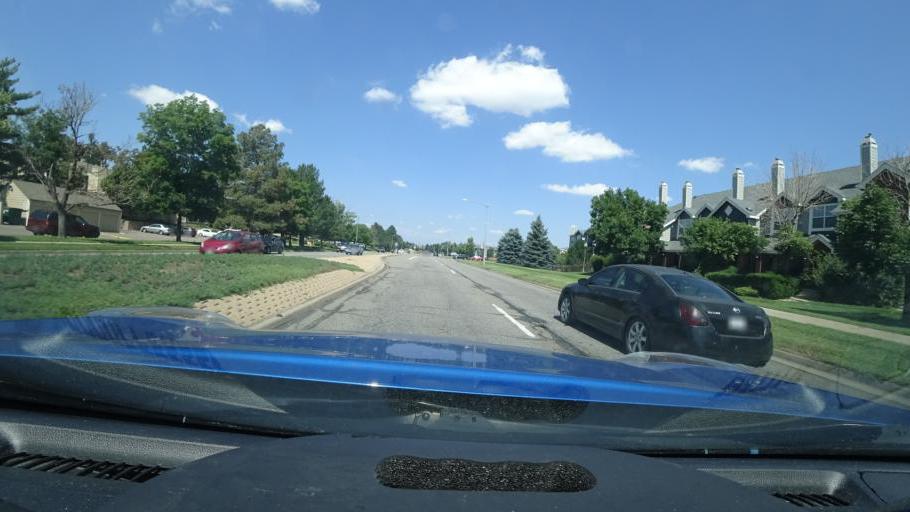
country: US
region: Colorado
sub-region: Arapahoe County
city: Glendale
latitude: 39.7090
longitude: -104.8887
